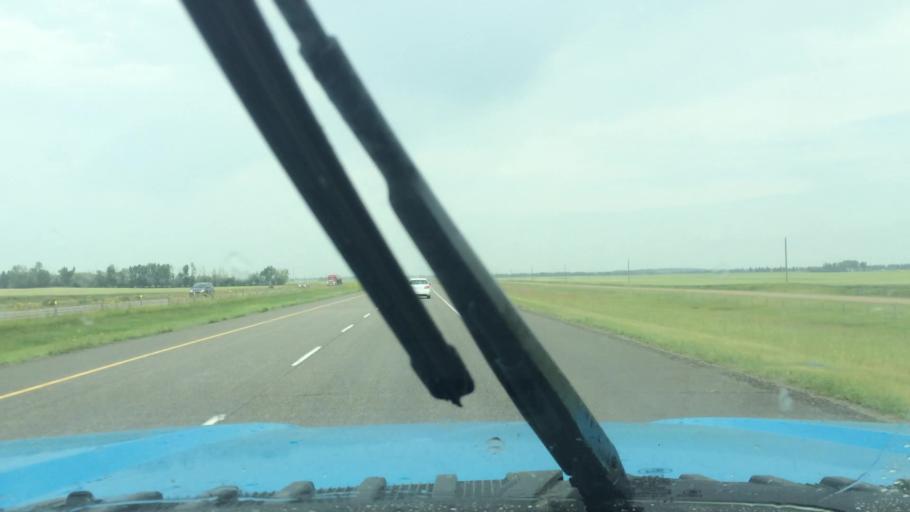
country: CA
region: Alberta
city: Olds
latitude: 51.7233
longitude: -114.0254
